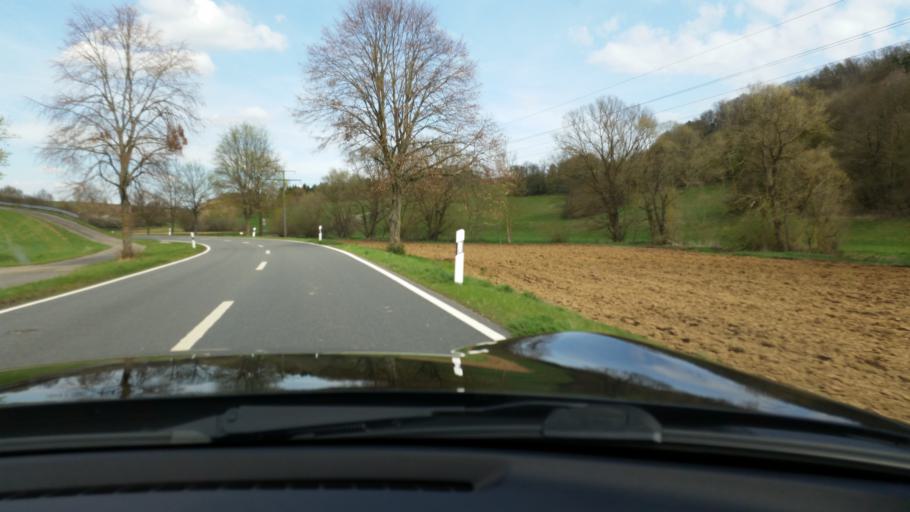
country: DE
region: Baden-Wuerttemberg
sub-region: Karlsruhe Region
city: Adelsheim
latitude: 49.3605
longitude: 9.3991
